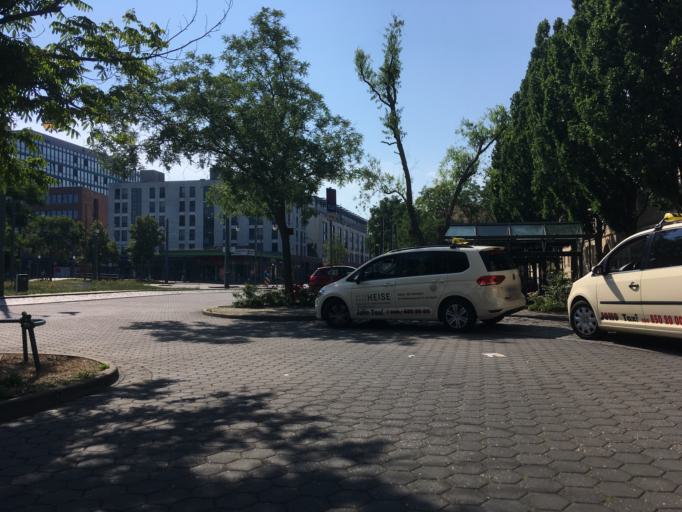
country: DE
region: Saxony-Anhalt
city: Dessau
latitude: 51.8392
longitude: 12.2354
